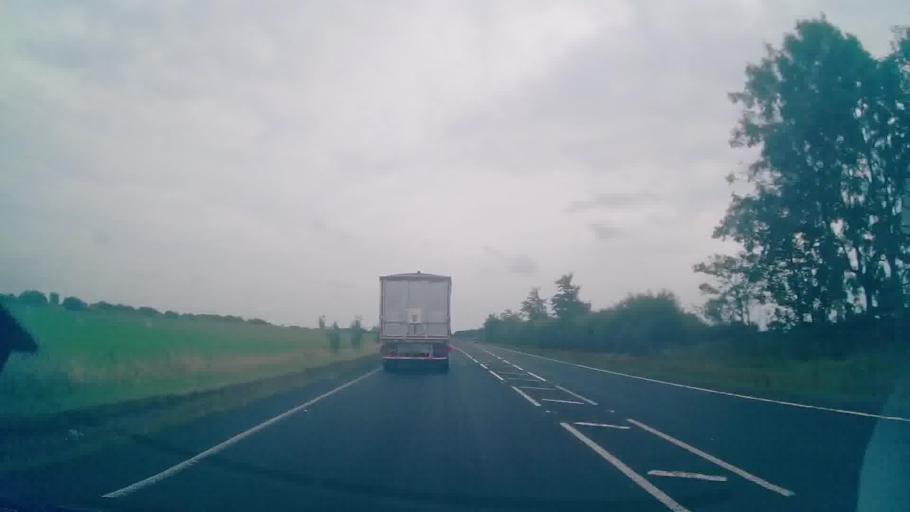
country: GB
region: Scotland
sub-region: Dumfries and Galloway
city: Gretna
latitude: 54.9956
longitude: -3.0925
